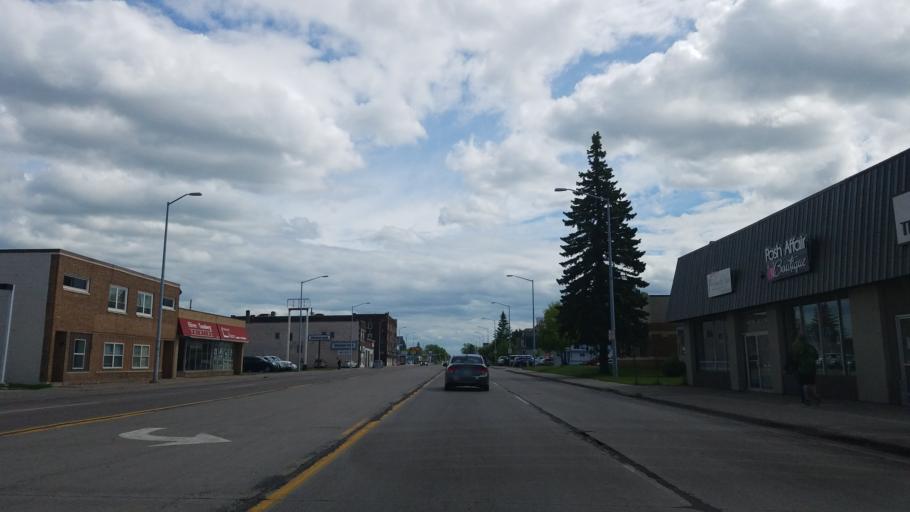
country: US
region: Wisconsin
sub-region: Douglas County
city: Superior
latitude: 46.7183
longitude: -92.1040
